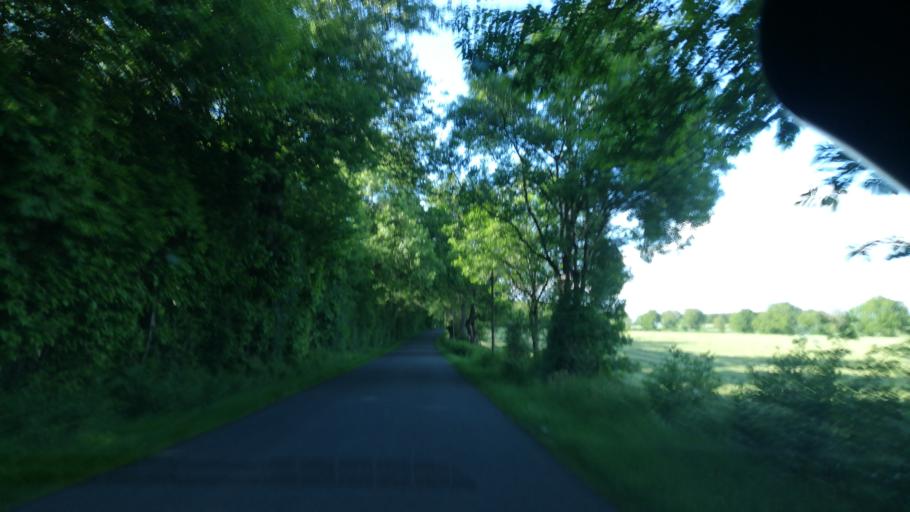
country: FR
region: Poitou-Charentes
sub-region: Departement des Deux-Sevres
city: Boisme
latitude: 46.7861
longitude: -0.4316
